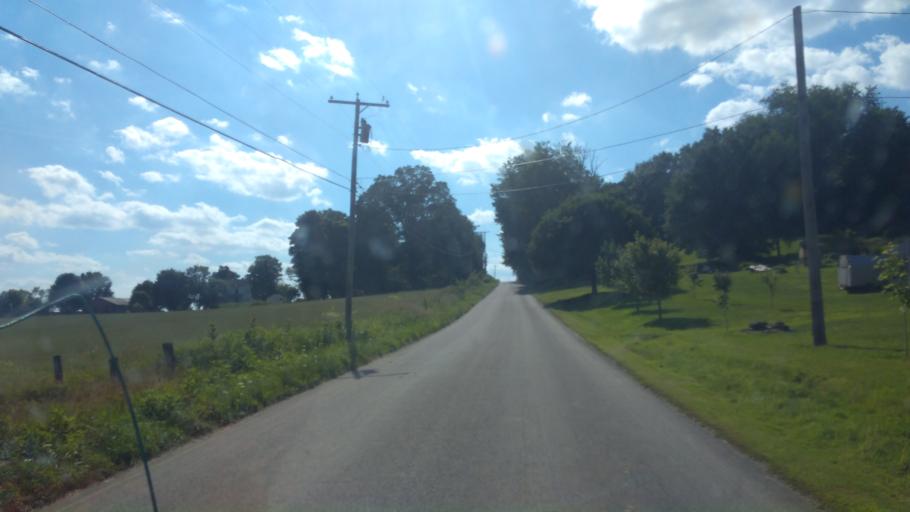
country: US
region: Ohio
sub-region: Stark County
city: Brewster
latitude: 40.7295
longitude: -81.6395
